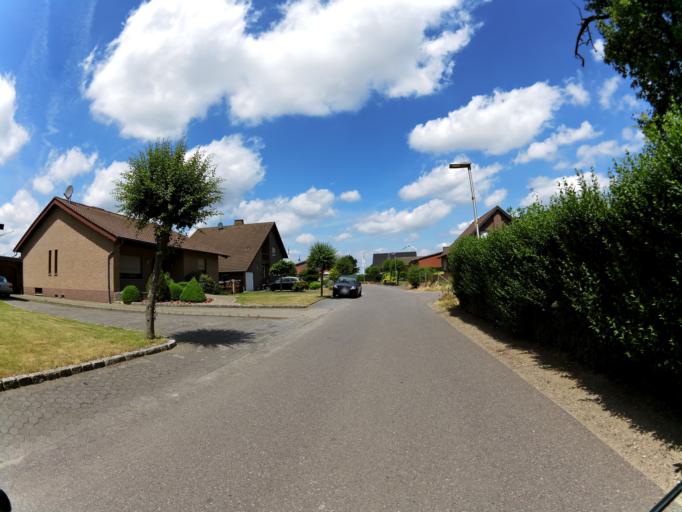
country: NL
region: Limburg
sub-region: Gemeente Echt-Susteren
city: Koningsbosch
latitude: 51.0283
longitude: 5.9872
